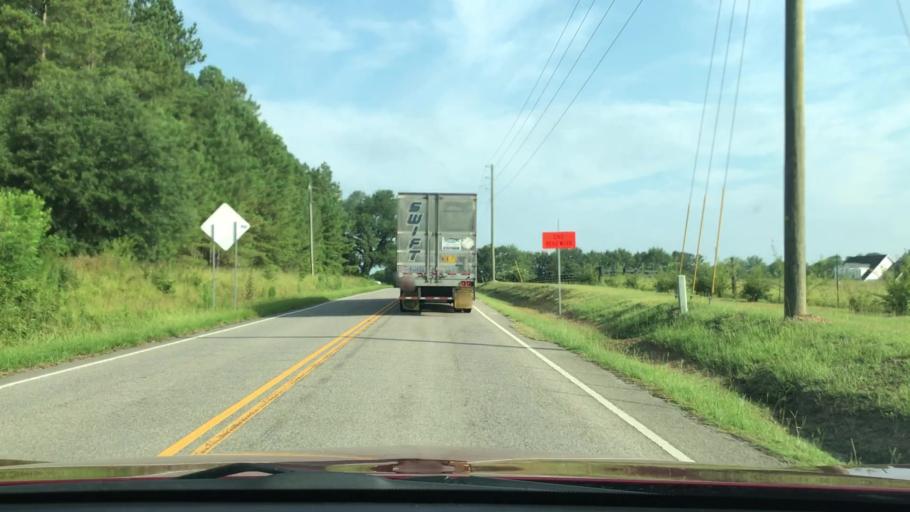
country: US
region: South Carolina
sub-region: Barnwell County
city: Blackville
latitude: 33.6051
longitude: -81.2664
